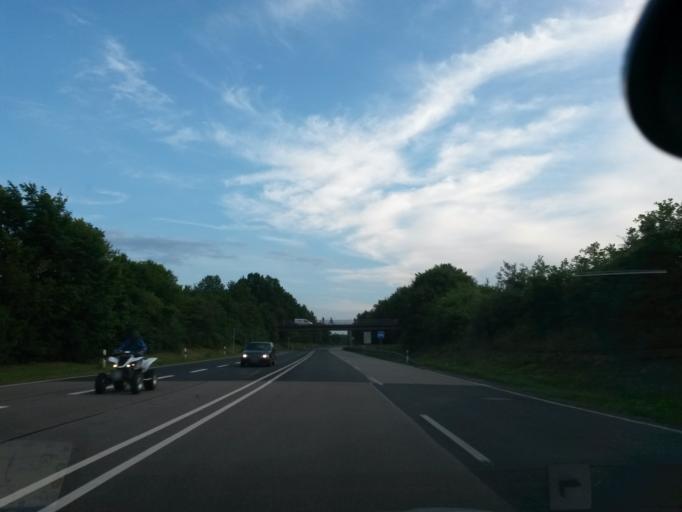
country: DE
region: Bavaria
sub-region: Upper Palatinate
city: Amberg
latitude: 49.4447
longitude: 11.8322
